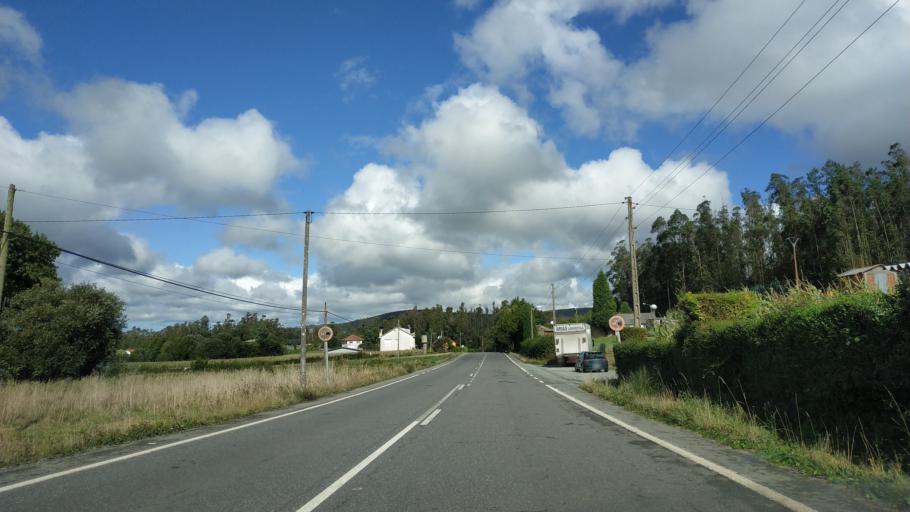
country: ES
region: Galicia
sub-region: Provincia da Coruna
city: Cerceda
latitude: 43.1991
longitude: -8.4639
